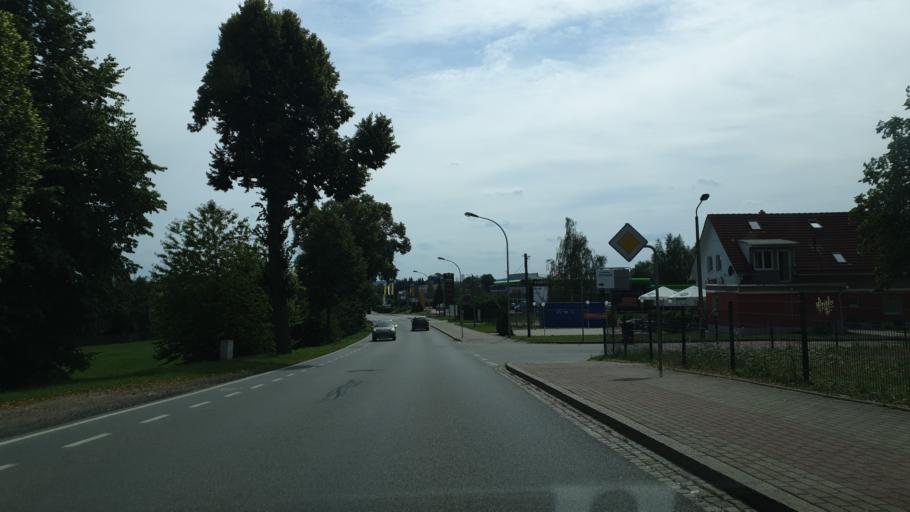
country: DE
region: Saxony
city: Oberlungwitz
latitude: 50.7919
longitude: 12.6983
